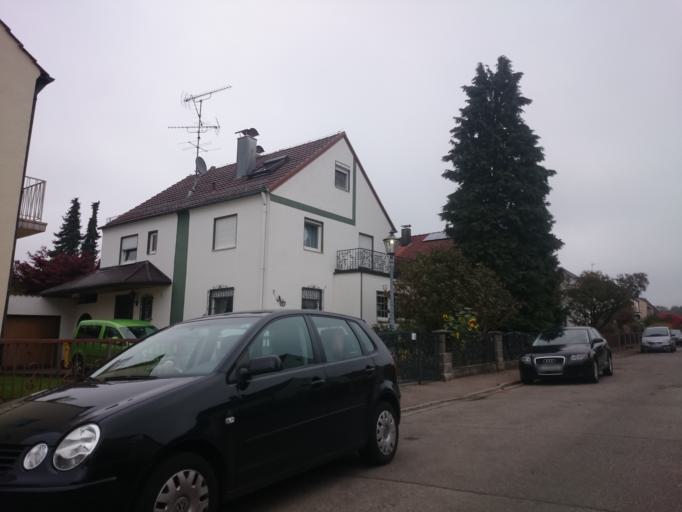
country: DE
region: Bavaria
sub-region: Swabia
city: Konigsbrunn
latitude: 48.2938
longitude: 10.8964
